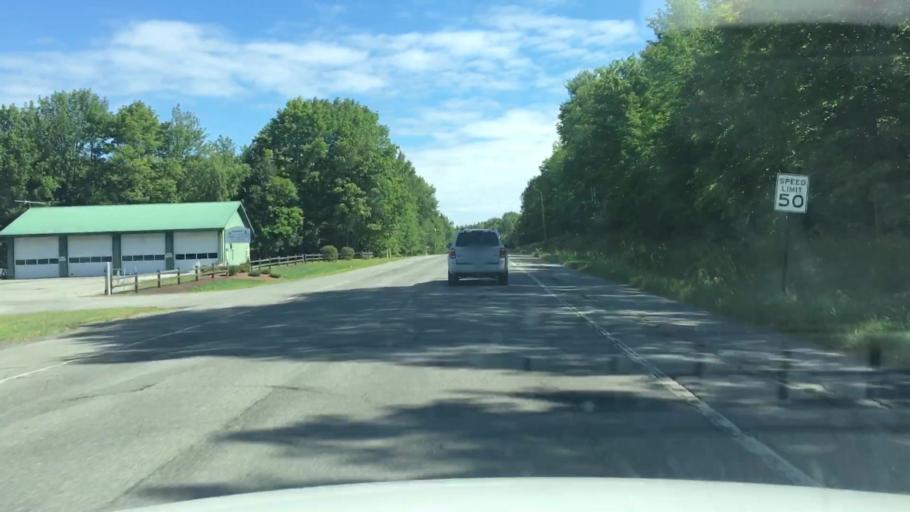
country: US
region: Maine
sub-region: Penobscot County
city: Dexter
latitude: 45.0492
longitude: -69.2663
